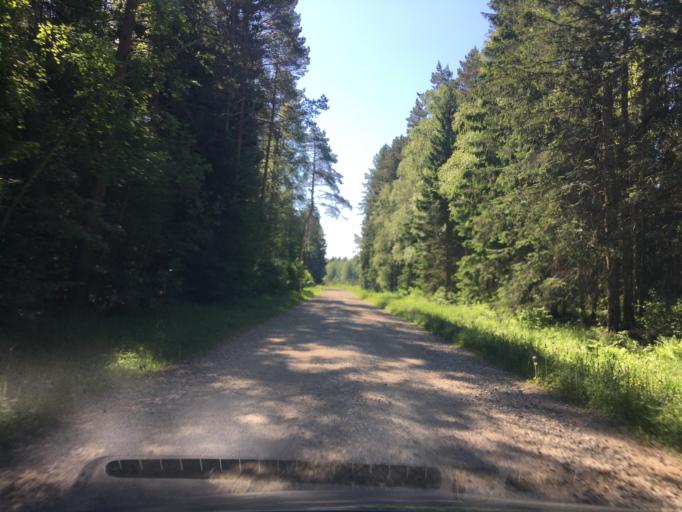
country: EE
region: Laeaene
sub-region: Lihula vald
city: Lihula
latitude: 58.6348
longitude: 23.7986
